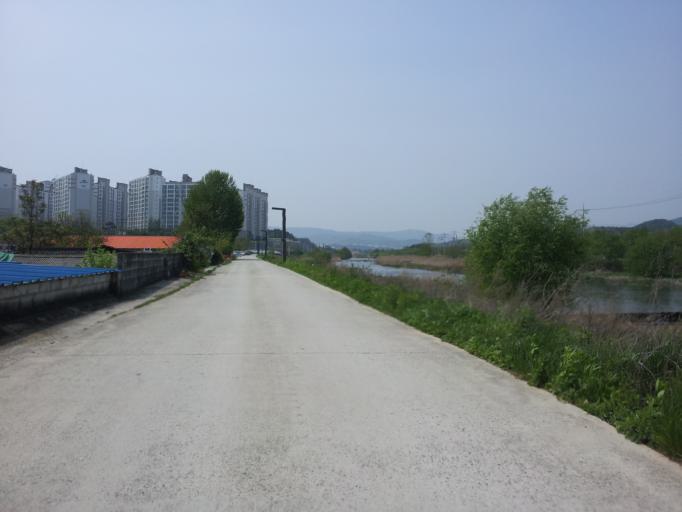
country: KR
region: Daejeon
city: Daejeon
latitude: 36.2670
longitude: 127.2772
